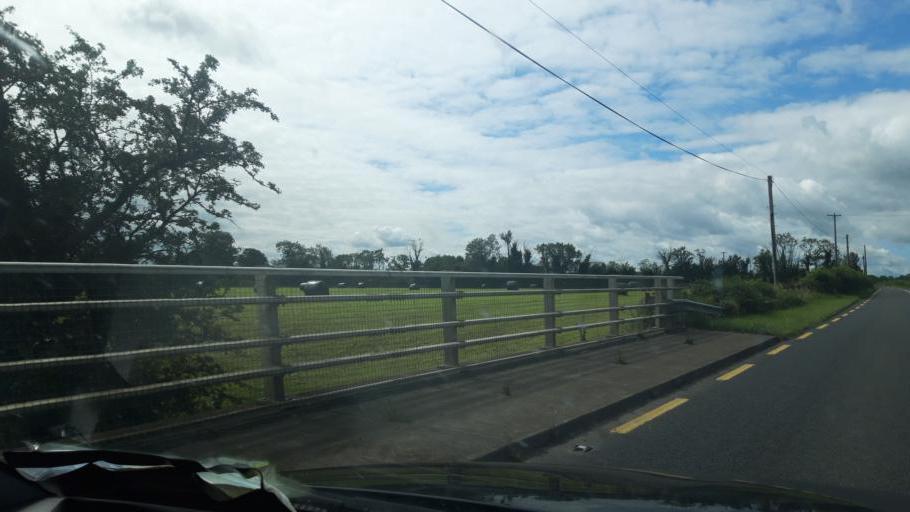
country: IE
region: Leinster
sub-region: Kilkenny
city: Callan
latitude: 52.5296
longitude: -7.4118
